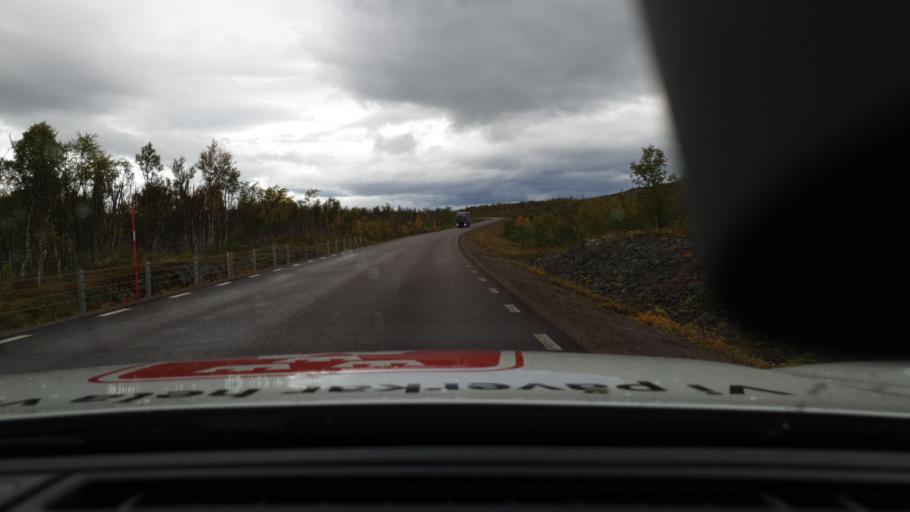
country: NO
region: Troms
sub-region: Bardu
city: Setermoen
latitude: 68.4264
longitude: 18.3435
